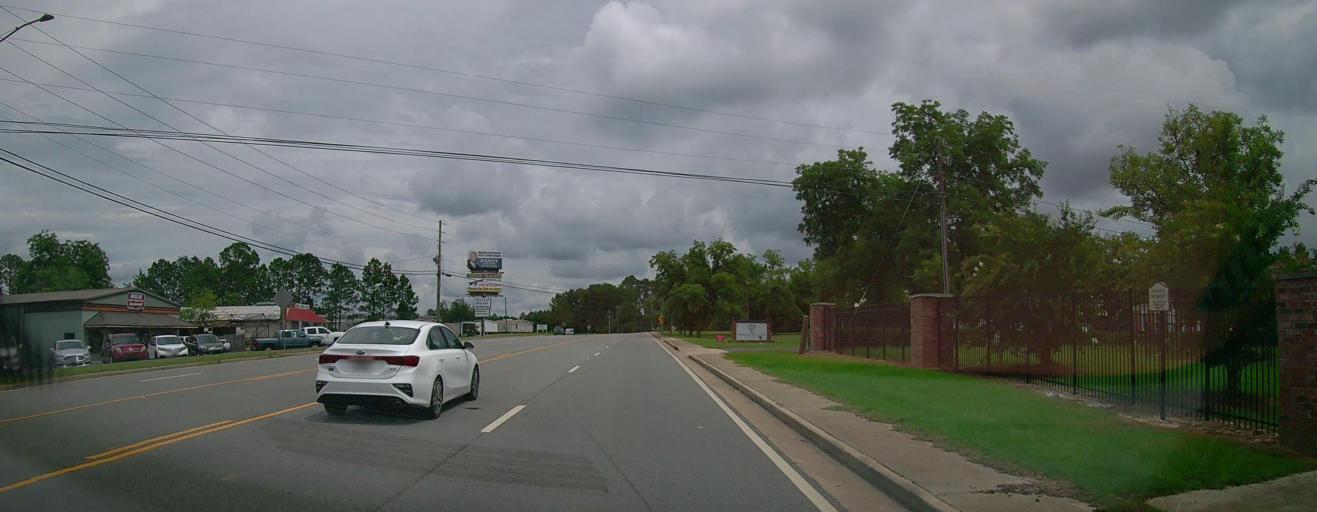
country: US
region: Georgia
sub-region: Telfair County
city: McRae
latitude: 32.0615
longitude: -82.8827
